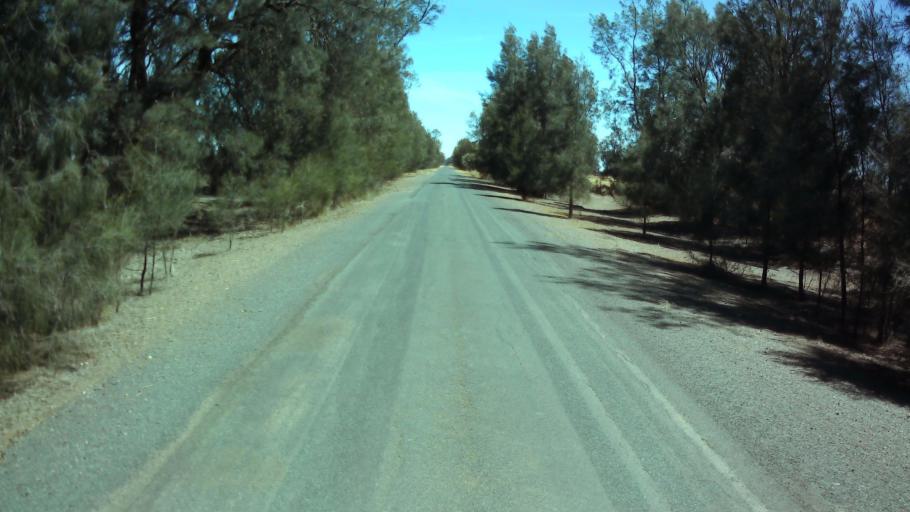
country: AU
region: New South Wales
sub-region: Weddin
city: Grenfell
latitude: -33.8854
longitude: 147.6892
